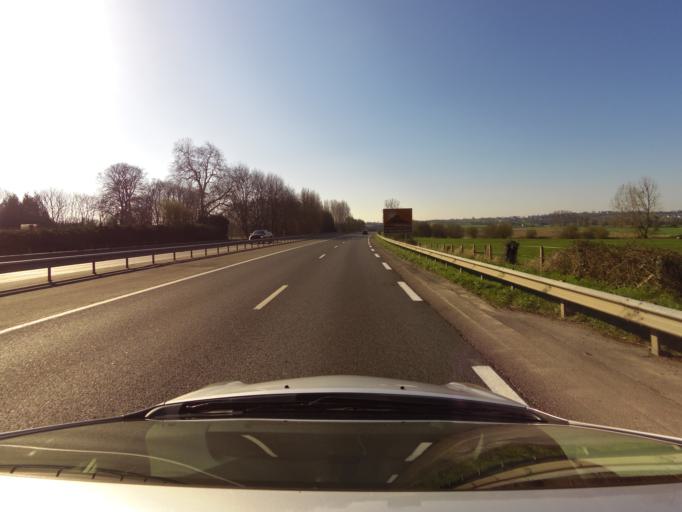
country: FR
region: Lower Normandy
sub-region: Departement de la Manche
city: Saint-Quentin-sur-le-Homme
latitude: 48.6417
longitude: -1.3424
